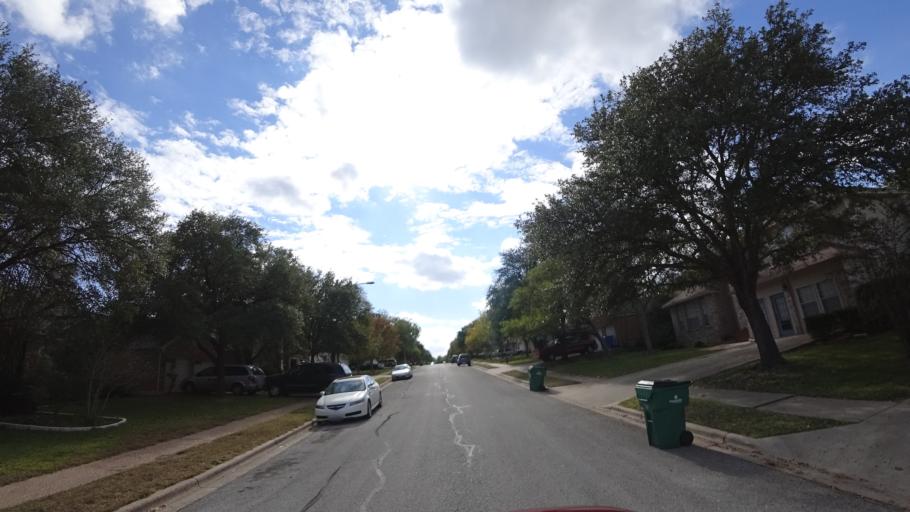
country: US
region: Texas
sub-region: Travis County
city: Pflugerville
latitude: 30.4395
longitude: -97.6343
